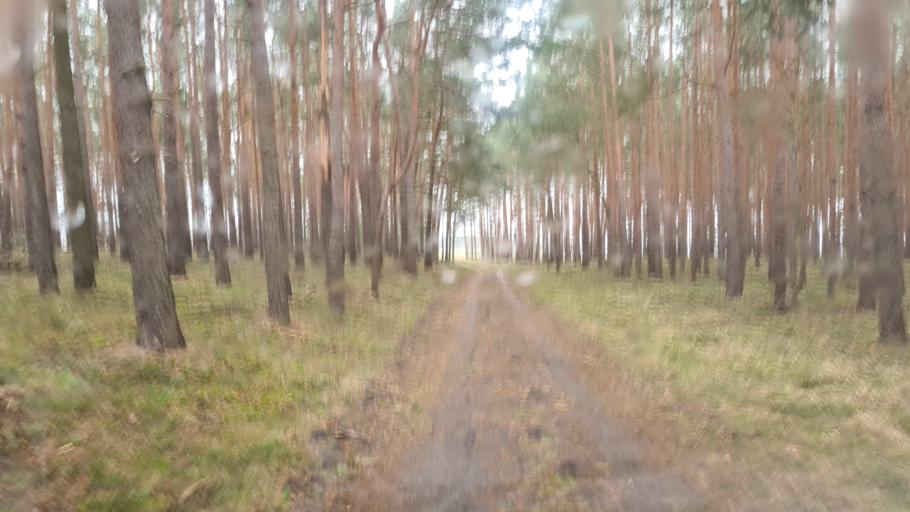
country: DE
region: Brandenburg
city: Bruck
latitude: 52.1590
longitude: 12.7194
